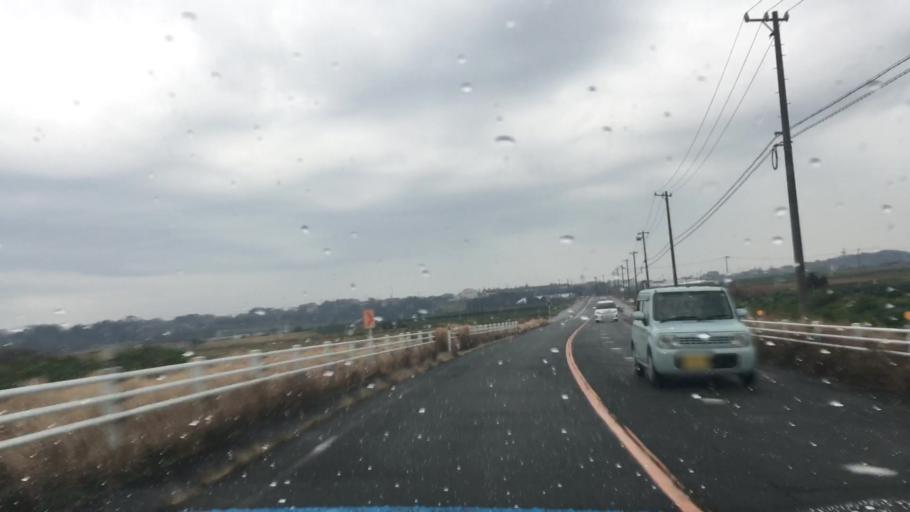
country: JP
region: Aichi
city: Toyohashi
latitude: 34.6743
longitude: 137.3910
